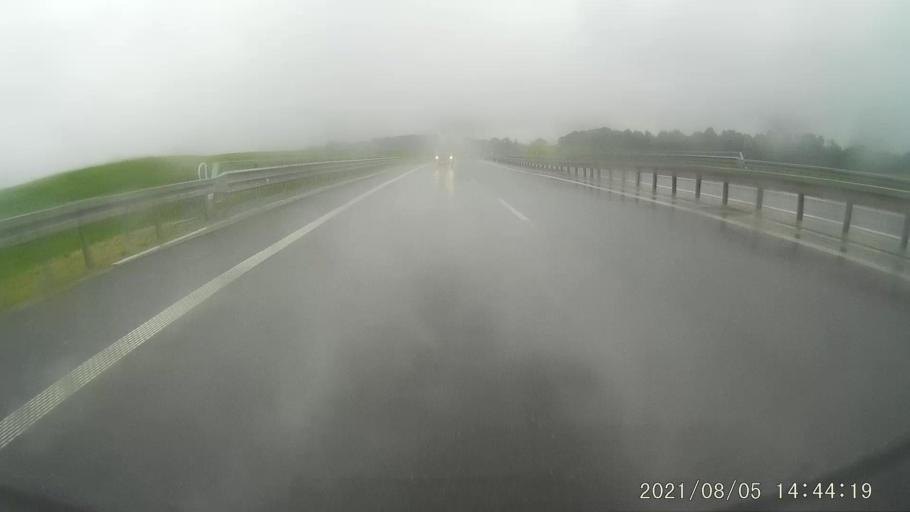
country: PL
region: Opole Voivodeship
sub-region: Powiat nyski
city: Nysa
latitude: 50.4932
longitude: 17.3802
